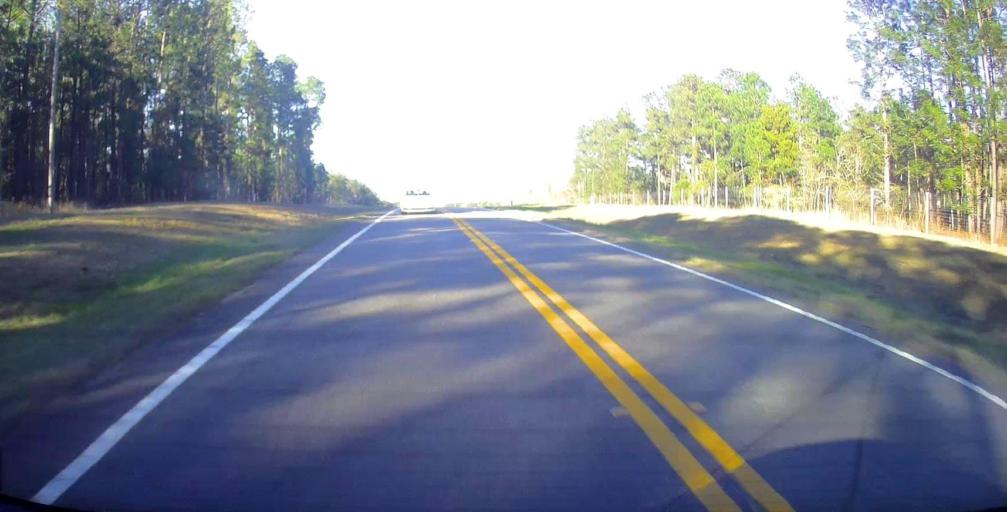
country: US
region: Georgia
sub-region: Taylor County
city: Butler
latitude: 32.4834
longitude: -84.3504
